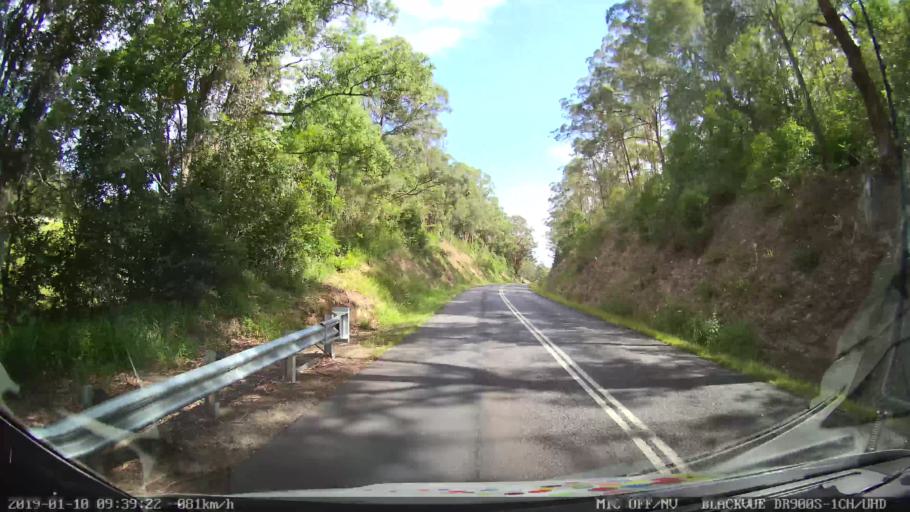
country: AU
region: New South Wales
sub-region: Coffs Harbour
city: Nana Glen
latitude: -30.1642
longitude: 153.0025
